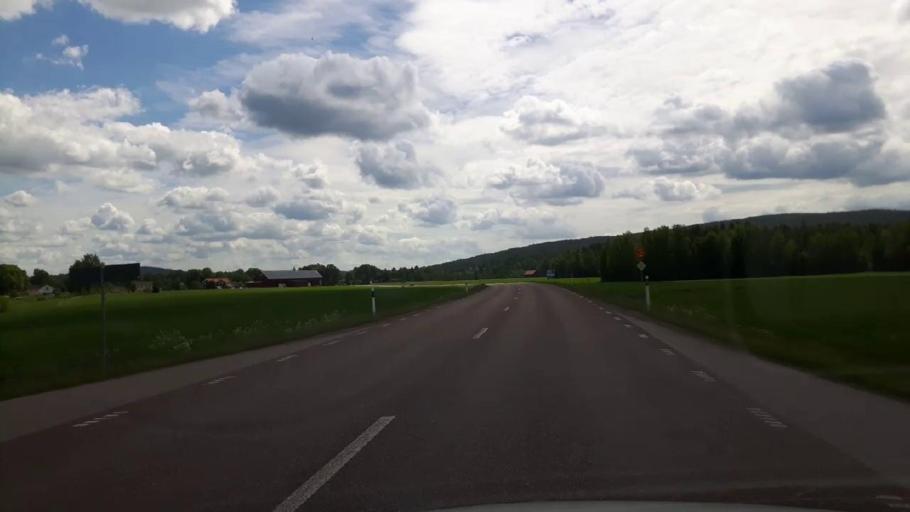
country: SE
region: Dalarna
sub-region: Saters Kommun
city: Saeter
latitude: 60.4024
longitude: 15.8741
